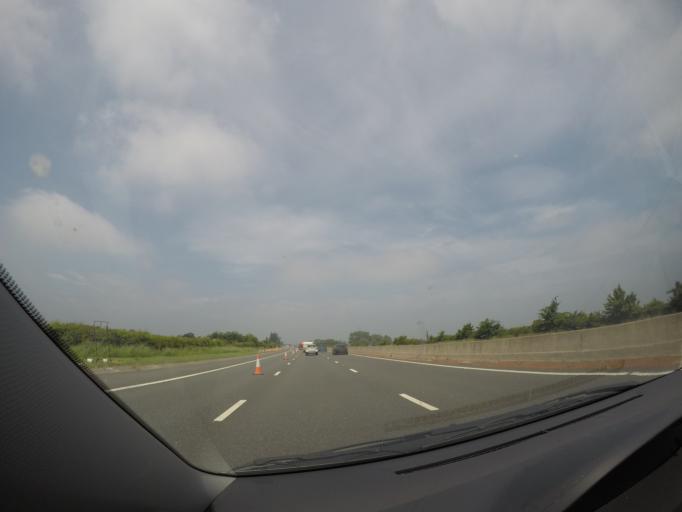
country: GB
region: England
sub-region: North Yorkshire
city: Bedale
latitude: 54.2451
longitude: -1.5026
